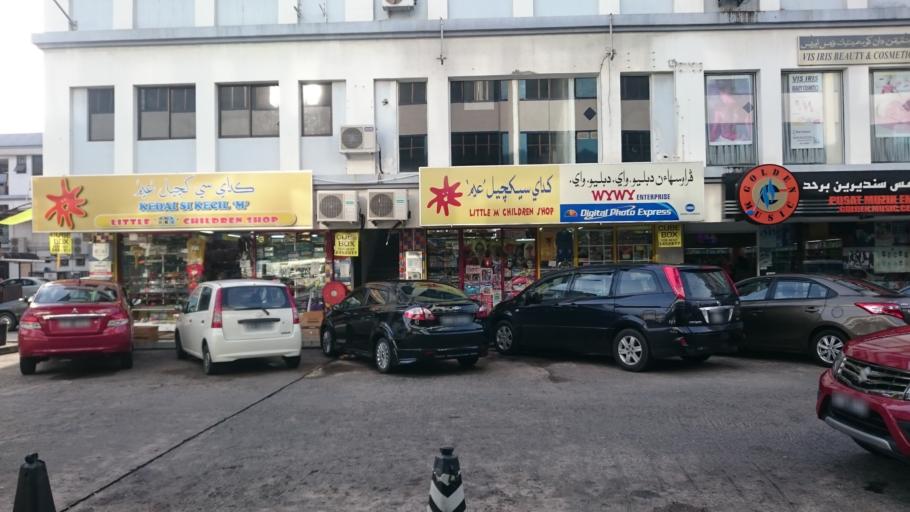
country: BN
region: Brunei and Muara
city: Bandar Seri Begawan
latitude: 4.9171
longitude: 114.9135
